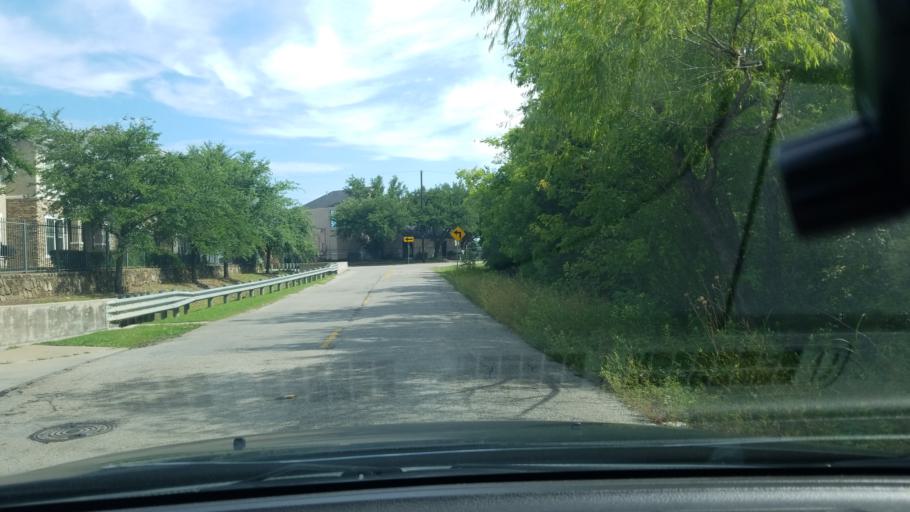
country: US
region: Texas
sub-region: Dallas County
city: Balch Springs
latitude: 32.7735
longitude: -96.6748
